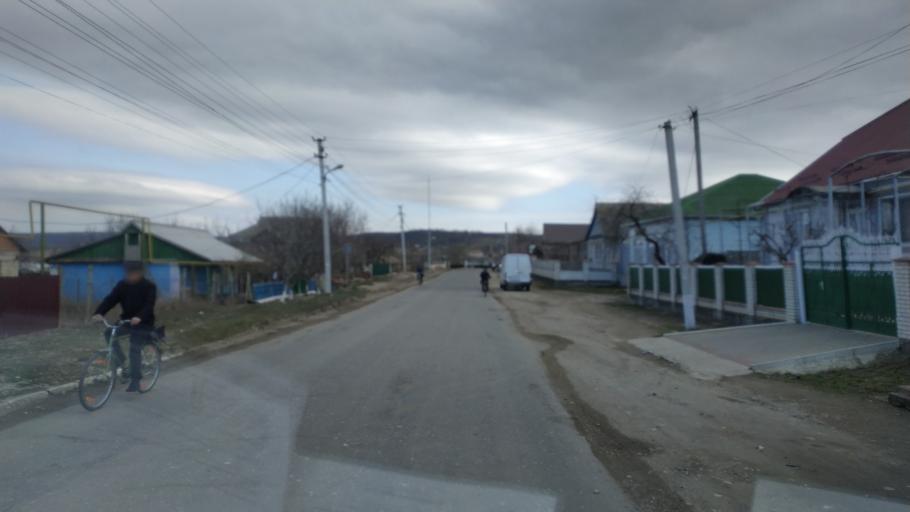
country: MD
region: Causeni
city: Causeni
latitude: 46.6441
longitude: 29.3927
